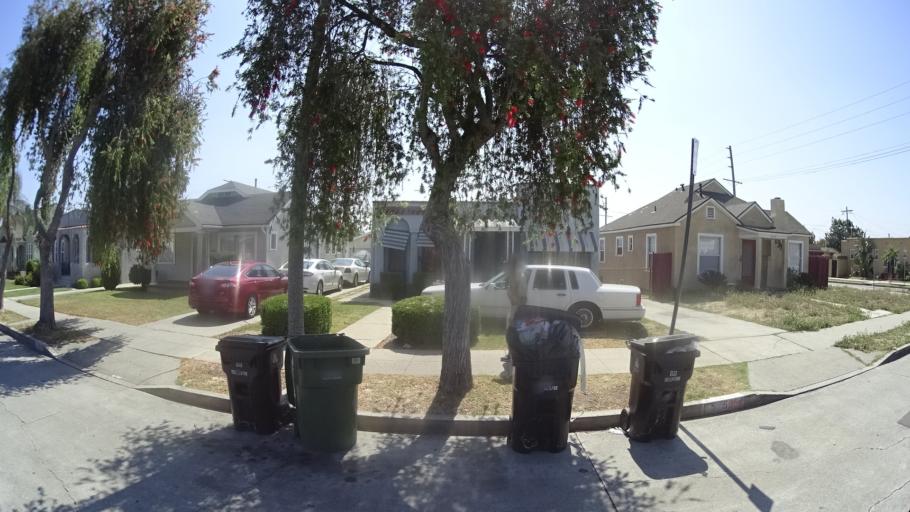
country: US
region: California
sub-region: Los Angeles County
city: View Park-Windsor Hills
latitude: 33.9857
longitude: -118.3235
